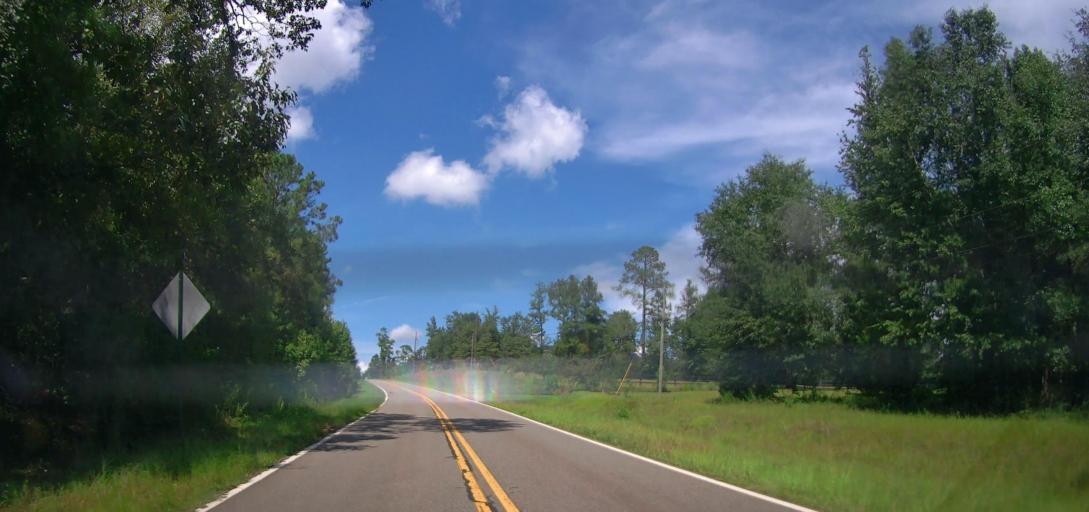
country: US
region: Georgia
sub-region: Peach County
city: Fort Valley
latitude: 32.5125
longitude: -83.8283
